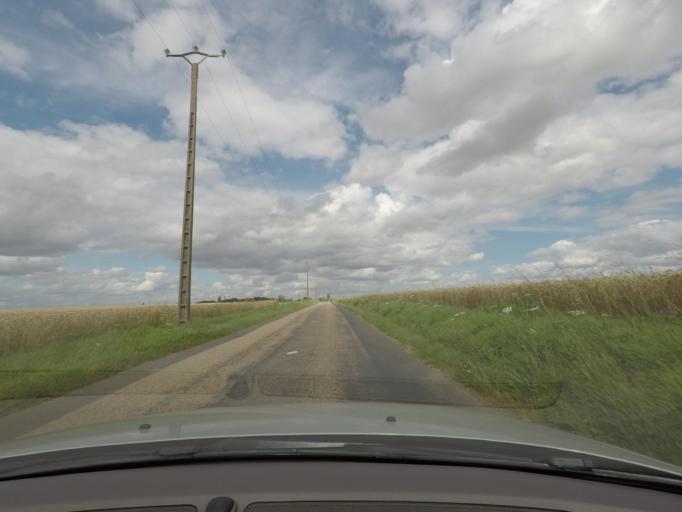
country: FR
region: Haute-Normandie
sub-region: Departement de l'Eure
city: Les Andelys
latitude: 49.1983
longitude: 1.4674
